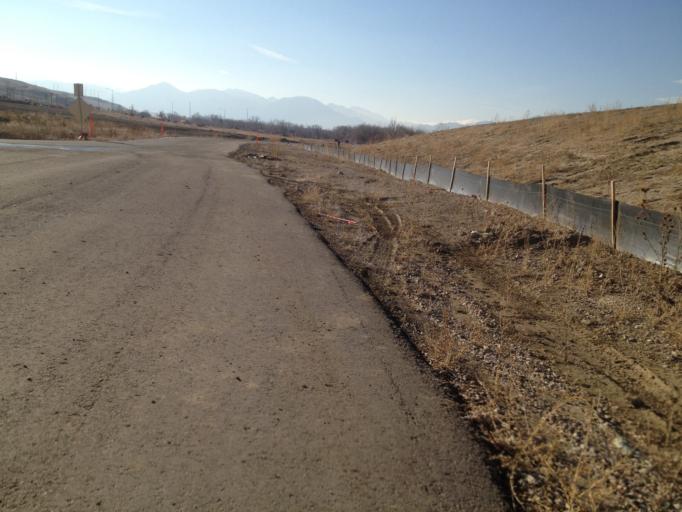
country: US
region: Colorado
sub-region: Boulder County
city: Superior
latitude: 39.9536
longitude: -105.1613
